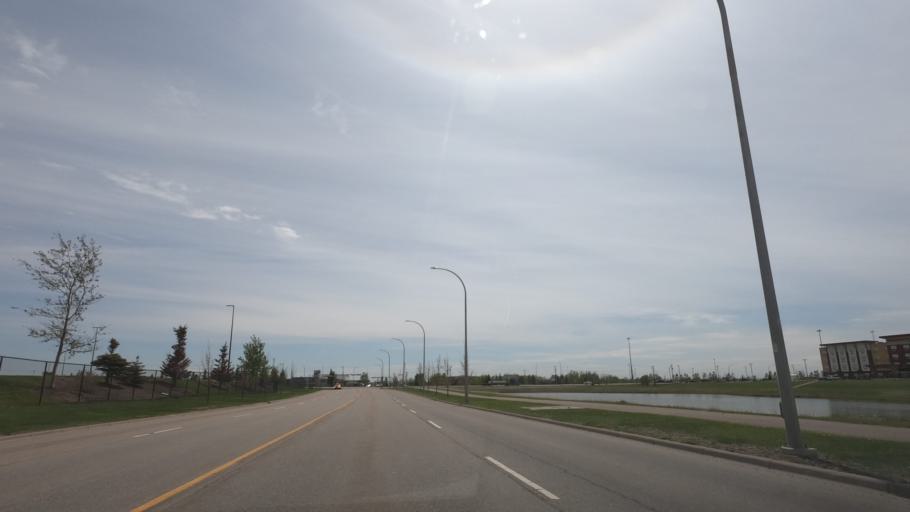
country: CA
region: Alberta
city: Airdrie
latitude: 51.3023
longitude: -113.9950
